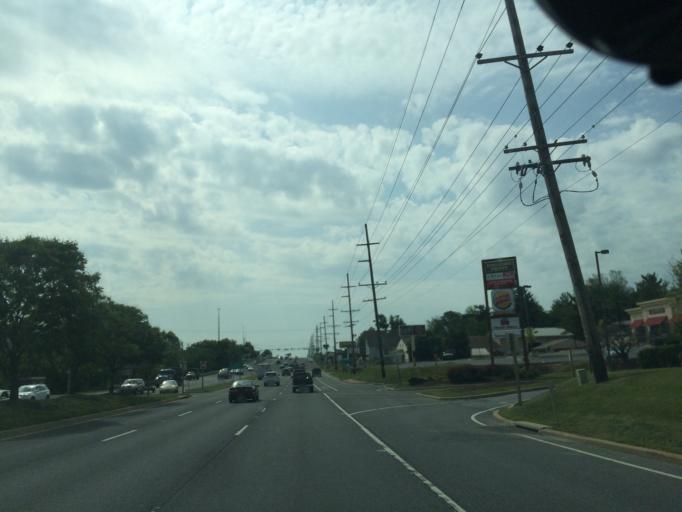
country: US
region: Maryland
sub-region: Carroll County
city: Westminster
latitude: 39.5631
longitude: -76.9721
